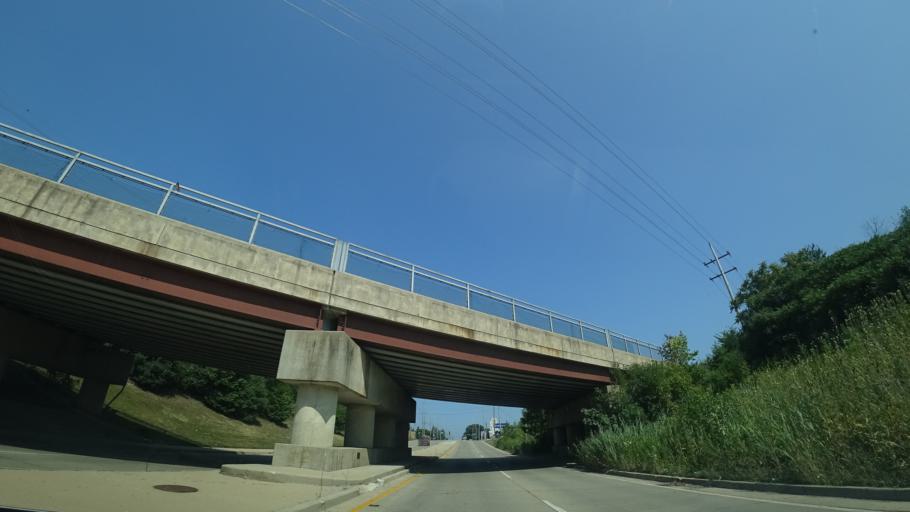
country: US
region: Illinois
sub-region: Cook County
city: Oak Lawn
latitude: 41.6906
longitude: -87.7531
